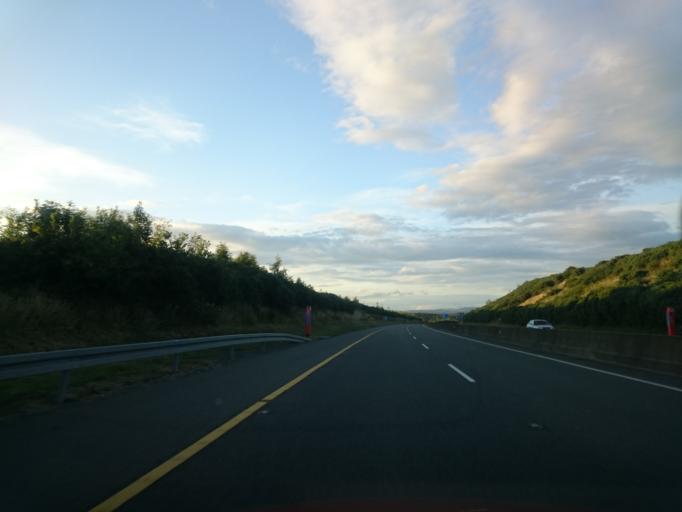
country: IE
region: Leinster
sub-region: Loch Garman
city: Gorey
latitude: 52.7042
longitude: -6.2620
